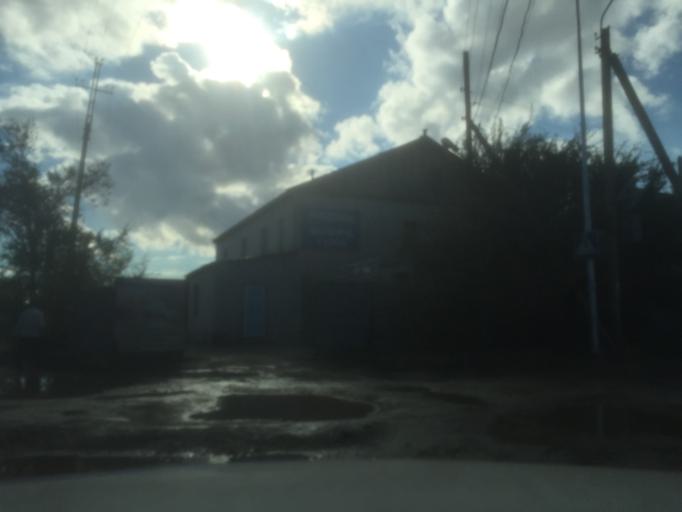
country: KZ
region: Astana Qalasy
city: Astana
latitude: 51.1876
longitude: 71.3934
